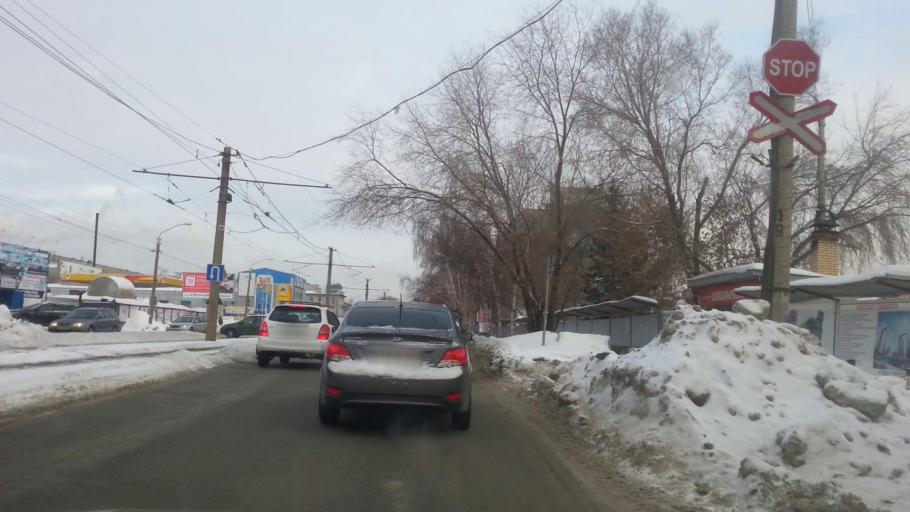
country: RU
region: Altai Krai
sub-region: Gorod Barnaulskiy
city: Barnaul
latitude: 53.3735
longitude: 83.7505
